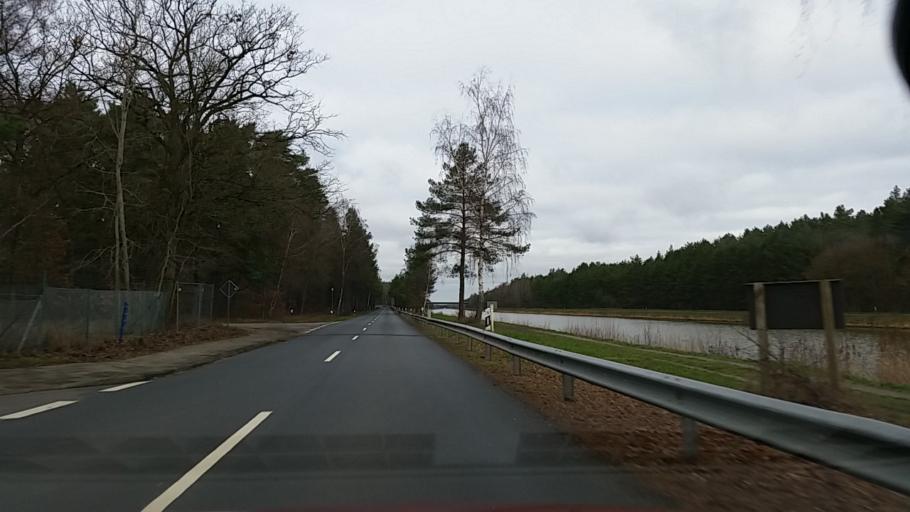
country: DE
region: Lower Saxony
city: Bodenteich
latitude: 52.8400
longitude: 10.6655
